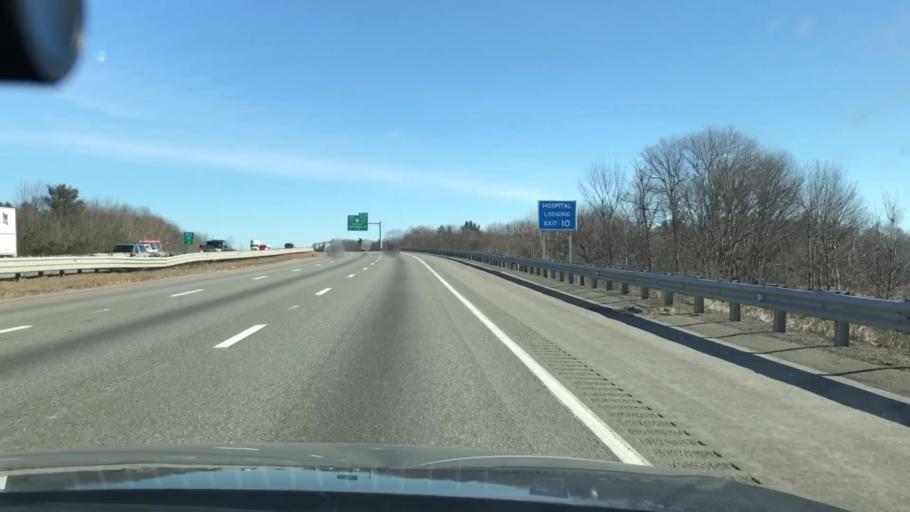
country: US
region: Massachusetts
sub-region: Worcester County
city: Auburn
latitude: 42.1865
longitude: -71.8763
